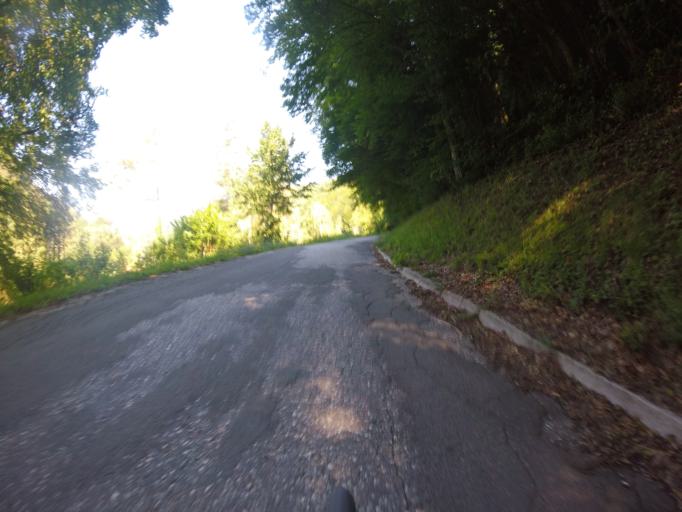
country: SI
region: Brezice
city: Brezice
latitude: 45.8368
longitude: 15.6076
